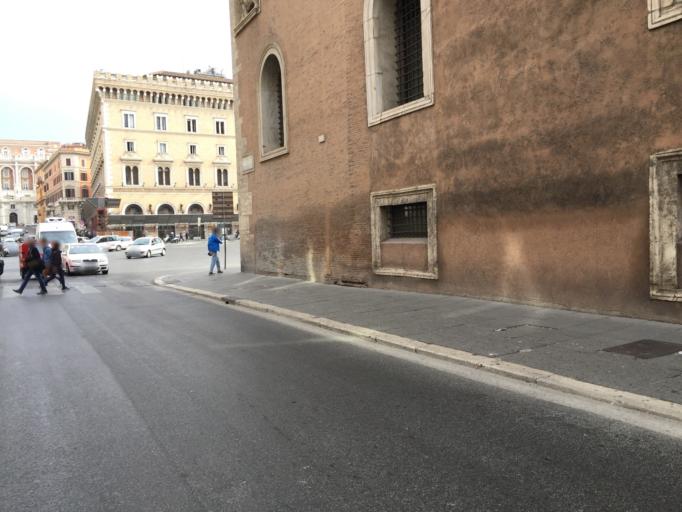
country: VA
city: Vatican City
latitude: 41.8969
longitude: 12.4803
